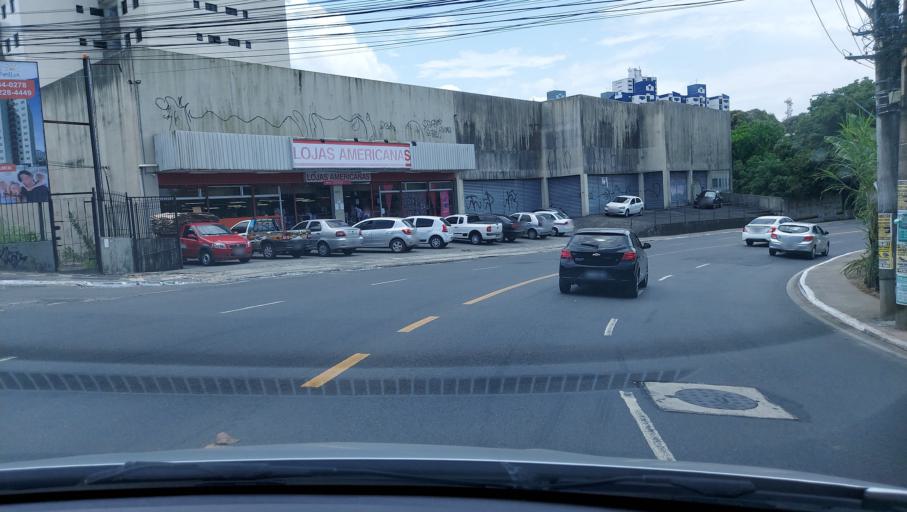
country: BR
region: Bahia
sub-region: Salvador
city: Salvador
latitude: -12.9578
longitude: -38.4671
